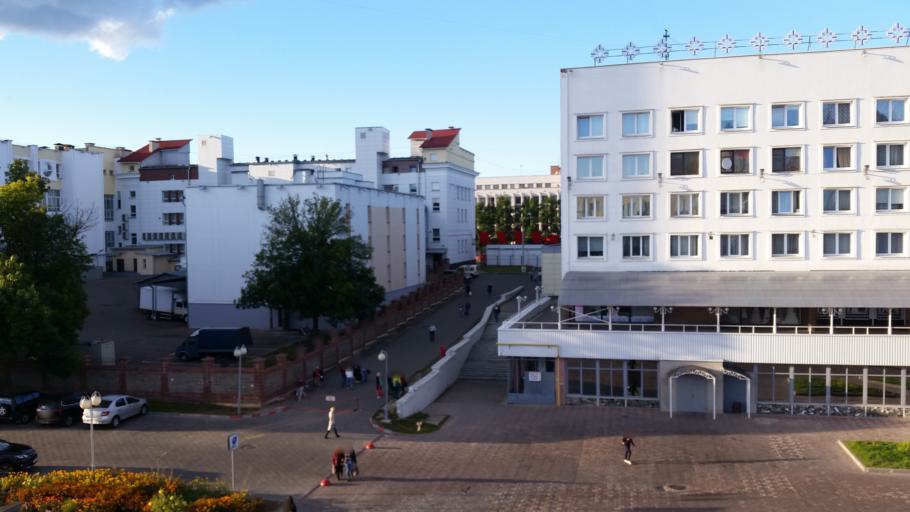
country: BY
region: Vitebsk
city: Vitebsk
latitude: 55.1914
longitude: 30.2043
